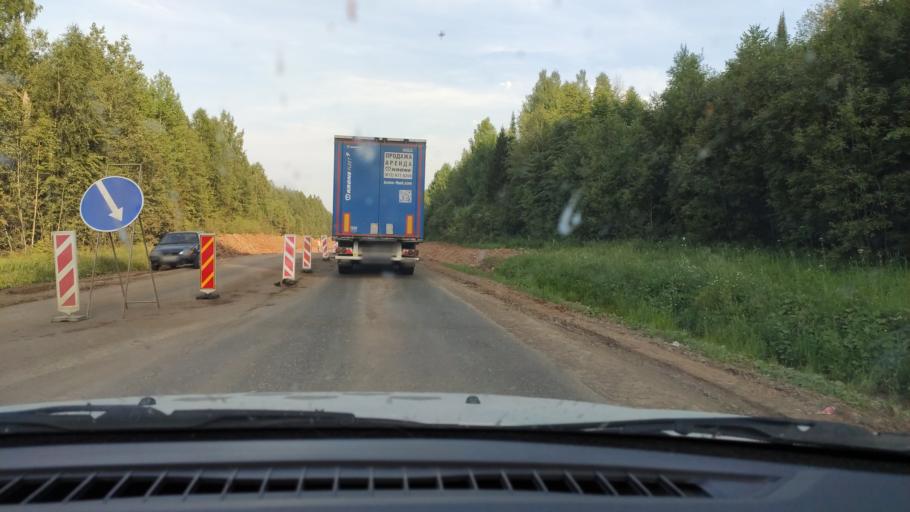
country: RU
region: Perm
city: Siva
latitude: 58.4901
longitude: 54.3588
